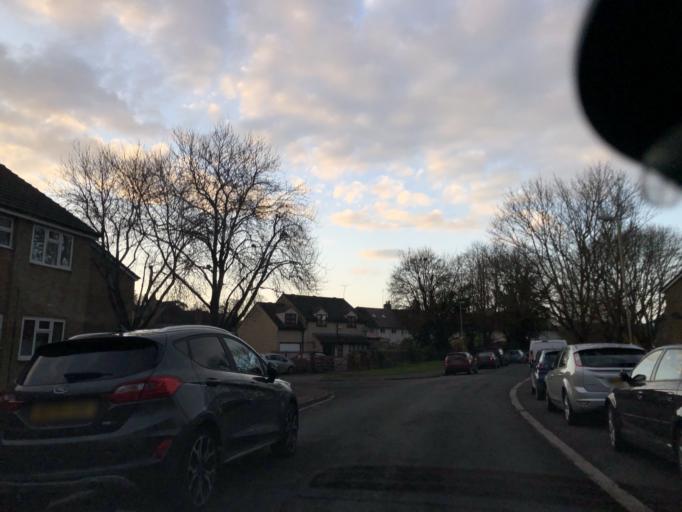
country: GB
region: England
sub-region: Oxfordshire
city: Witney
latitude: 51.7840
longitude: -1.4947
